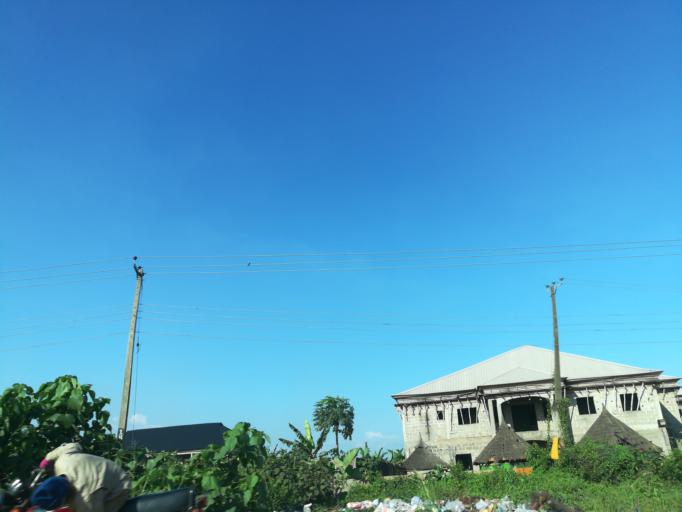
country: NG
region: Lagos
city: Ikorodu
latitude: 6.5690
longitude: 3.5332
